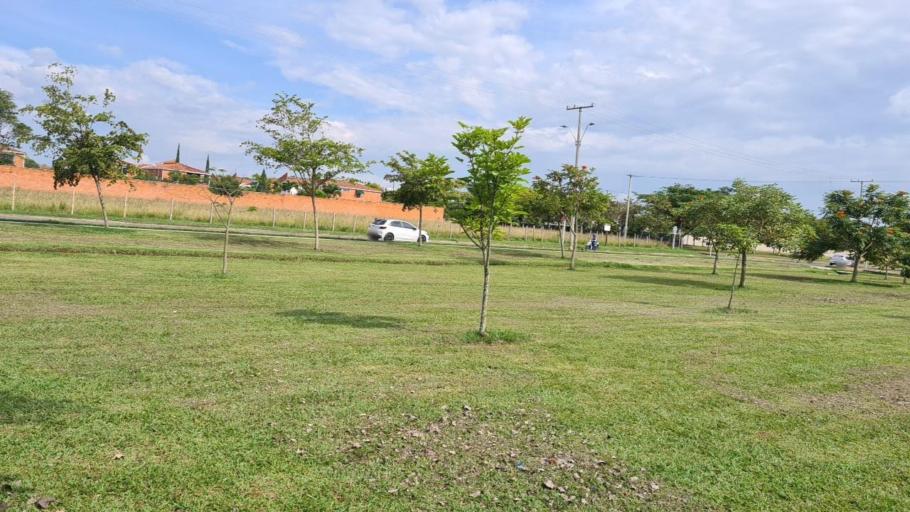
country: CO
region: Valle del Cauca
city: Jamundi
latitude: 3.2567
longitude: -76.5636
